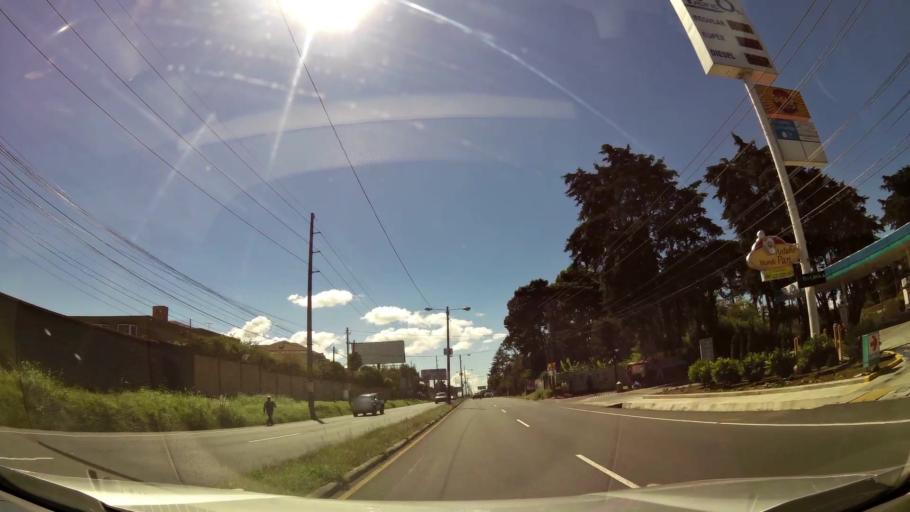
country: GT
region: Guatemala
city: Santa Catarina Pinula
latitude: 14.5234
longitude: -90.4691
